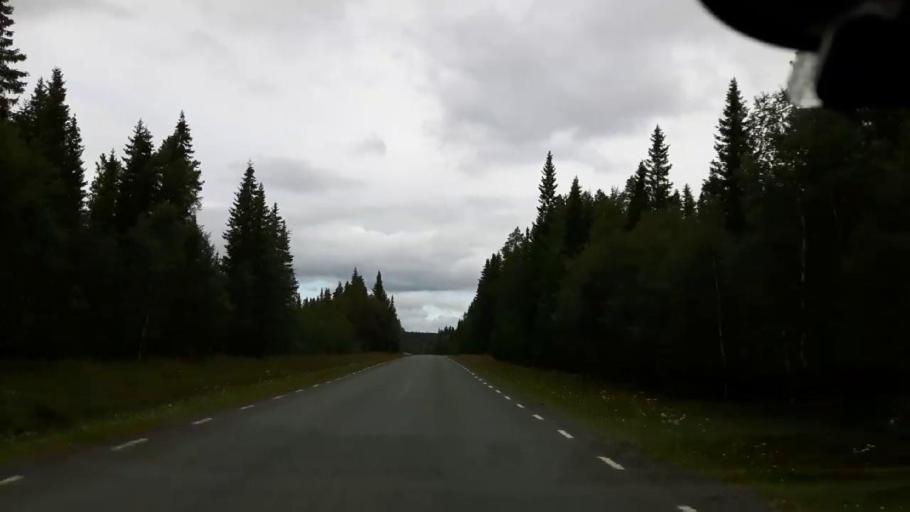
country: SE
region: Jaemtland
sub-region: Krokoms Kommun
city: Valla
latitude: 63.5587
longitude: 13.8495
